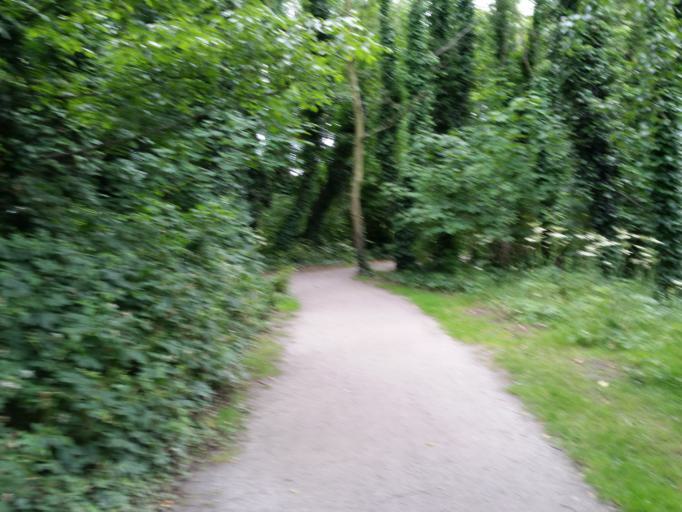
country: GB
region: Northern Ireland
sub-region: Castlereagh District
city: Castlereagh
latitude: 54.6083
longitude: -5.8891
